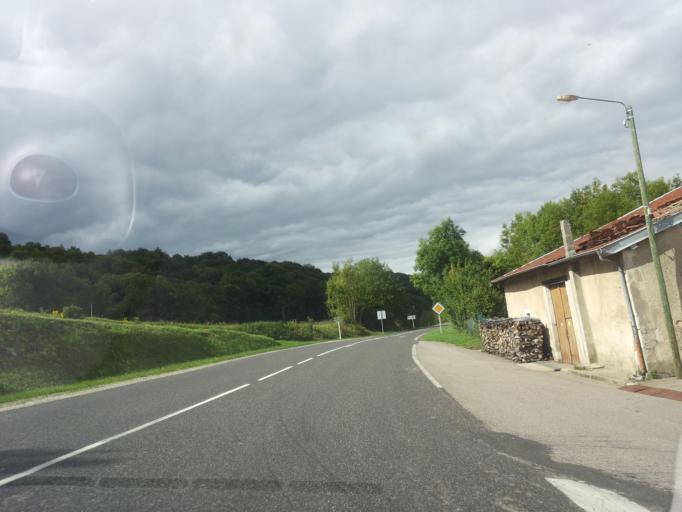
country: FR
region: Lorraine
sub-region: Departement de la Meuse
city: Ligny-en-Barrois
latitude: 48.6351
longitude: 5.3788
